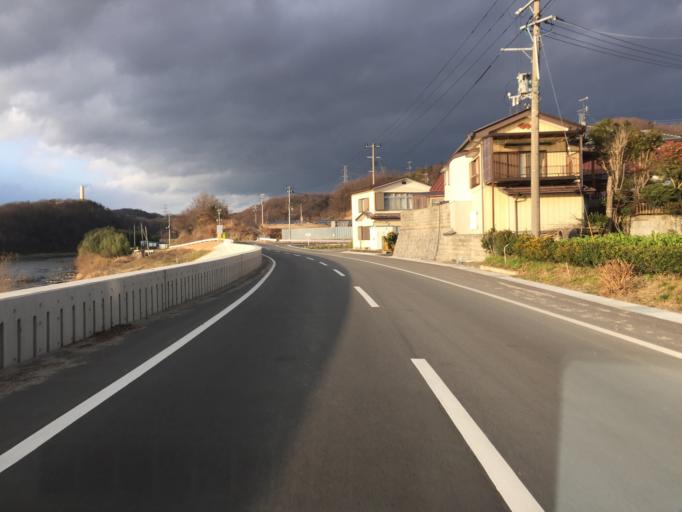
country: JP
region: Fukushima
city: Motomiya
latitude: 37.5222
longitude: 140.4161
